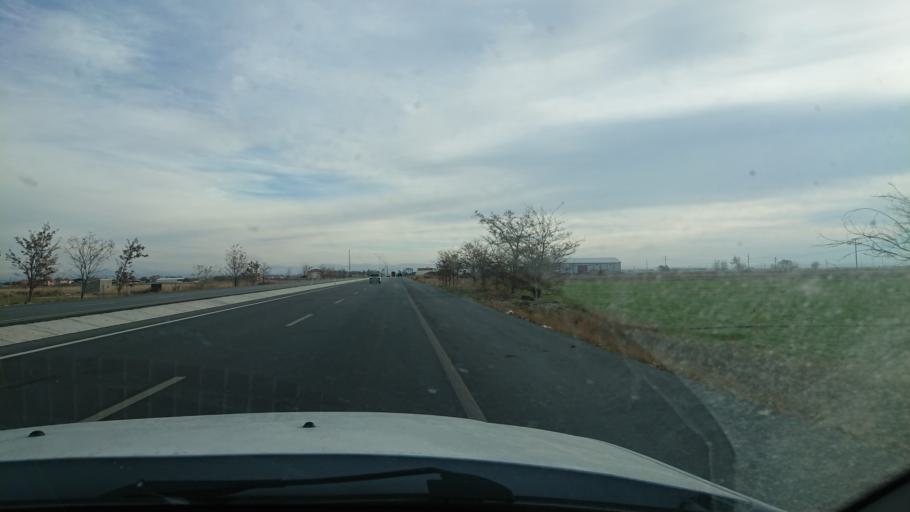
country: TR
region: Aksaray
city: Yesilova
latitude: 38.2887
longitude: 33.7497
